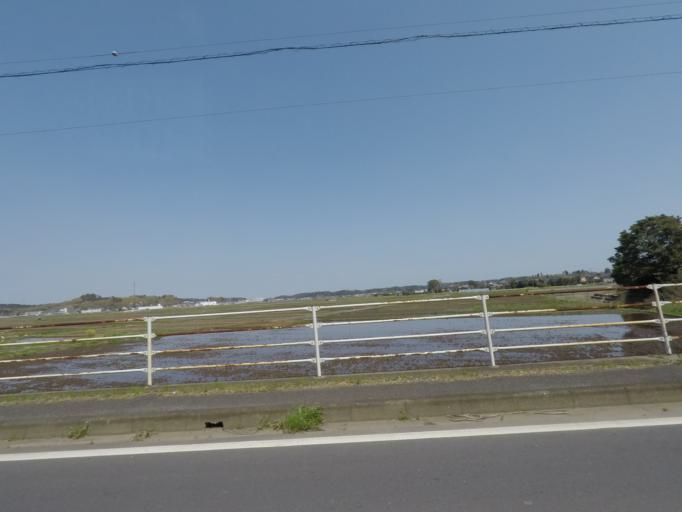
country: JP
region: Chiba
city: Yokaichiba
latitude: 35.7193
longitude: 140.4623
